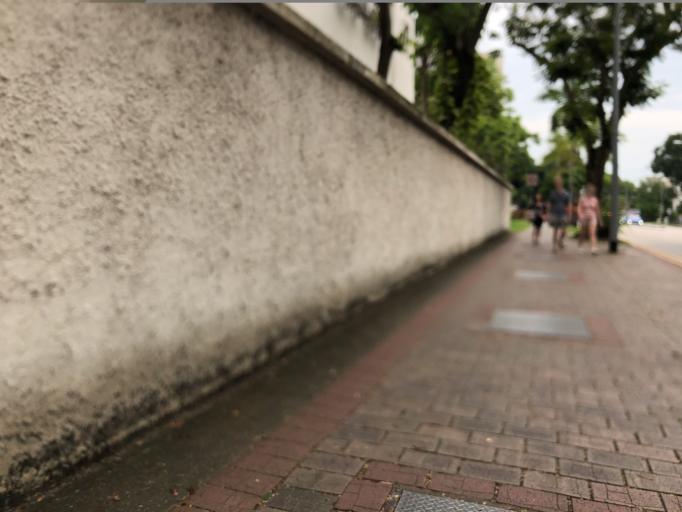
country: SG
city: Singapore
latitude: 1.3141
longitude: 103.8943
